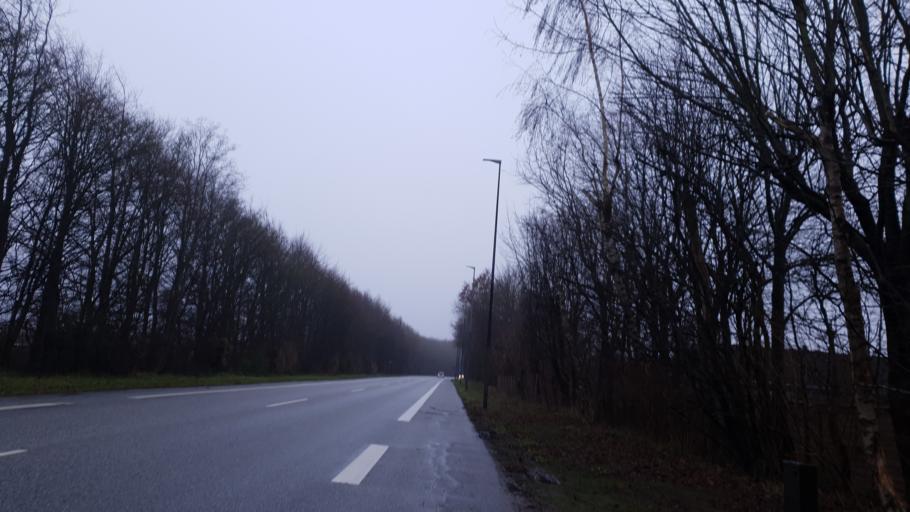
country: DK
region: Central Jutland
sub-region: Hedensted Kommune
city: Hedensted
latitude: 55.7892
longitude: 9.6996
